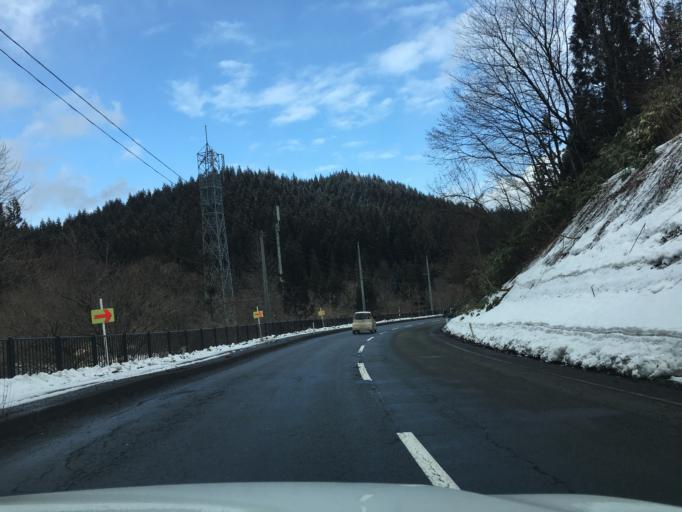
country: JP
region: Akita
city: Takanosu
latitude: 39.9899
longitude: 140.2461
